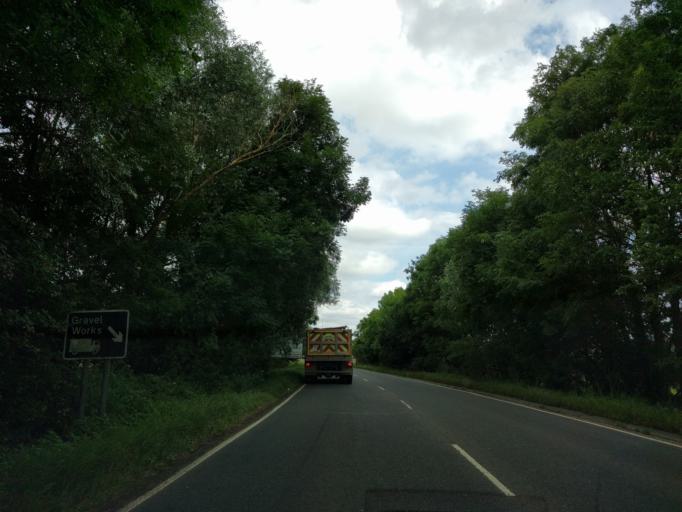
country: GB
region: England
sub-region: Cambridgeshire
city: Needingworth
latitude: 52.3302
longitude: -0.0595
